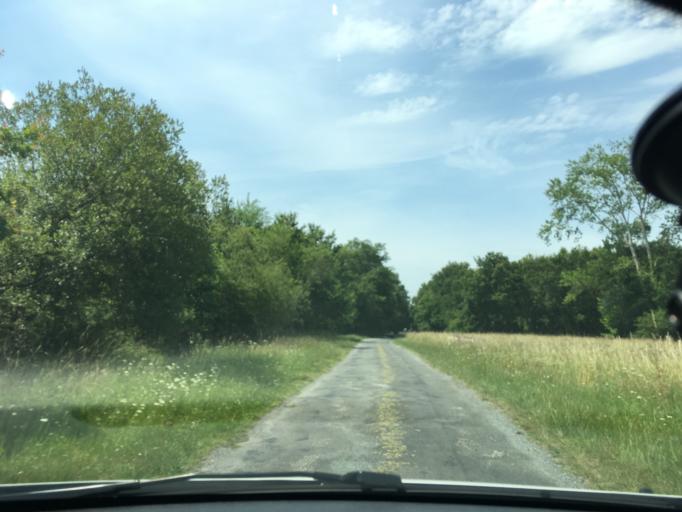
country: FR
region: Aquitaine
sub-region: Departement de la Gironde
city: Lesparre-Medoc
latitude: 45.2824
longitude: -0.9029
